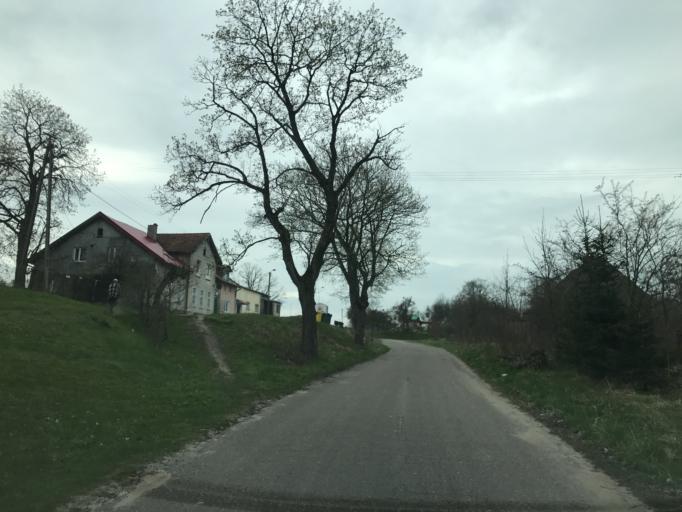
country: PL
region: Warmian-Masurian Voivodeship
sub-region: Powiat olsztynski
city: Olsztynek
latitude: 53.6265
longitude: 20.2198
